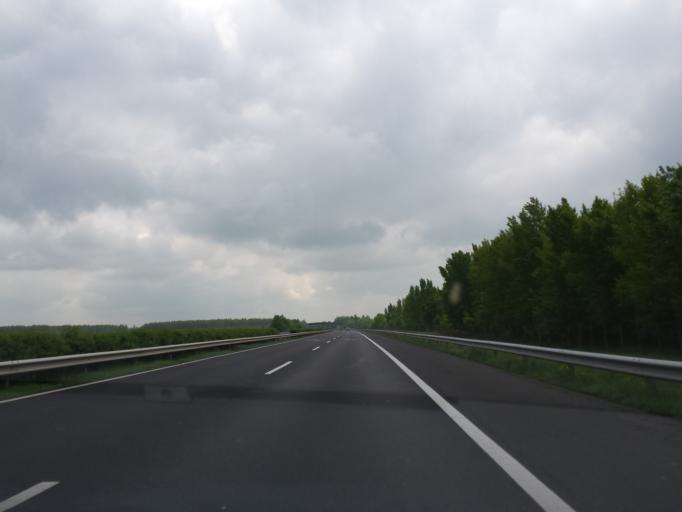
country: HU
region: Gyor-Moson-Sopron
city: Kimle
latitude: 47.8053
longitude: 17.3017
